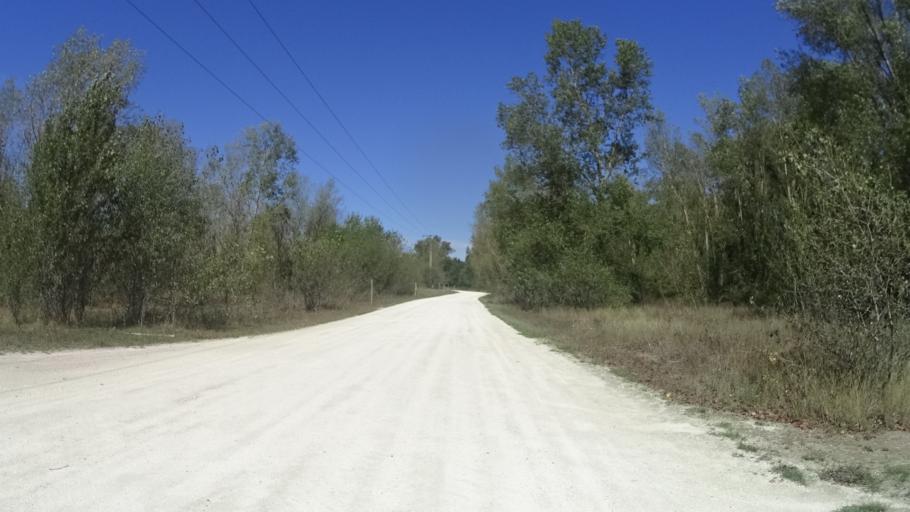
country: FR
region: Centre
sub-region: Departement du Loiret
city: Bonny-sur-Loire
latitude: 47.5444
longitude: 2.8358
